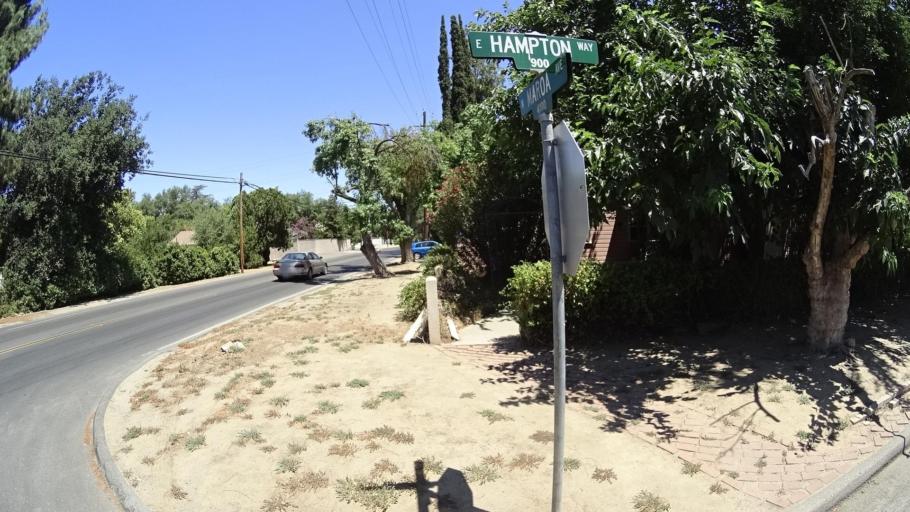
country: US
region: California
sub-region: Fresno County
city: Fresno
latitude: 36.7921
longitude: -119.7994
